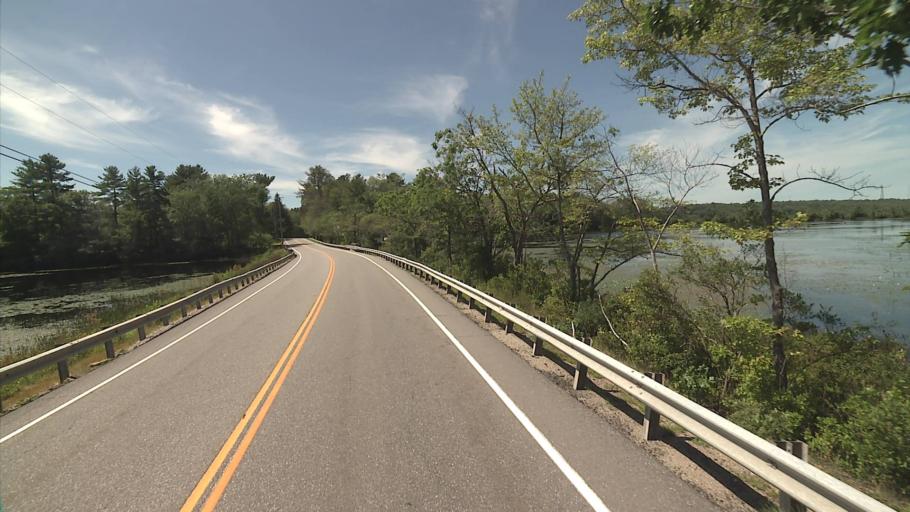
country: US
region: Rhode Island
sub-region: Providence County
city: Foster
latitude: 41.8491
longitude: -71.8009
